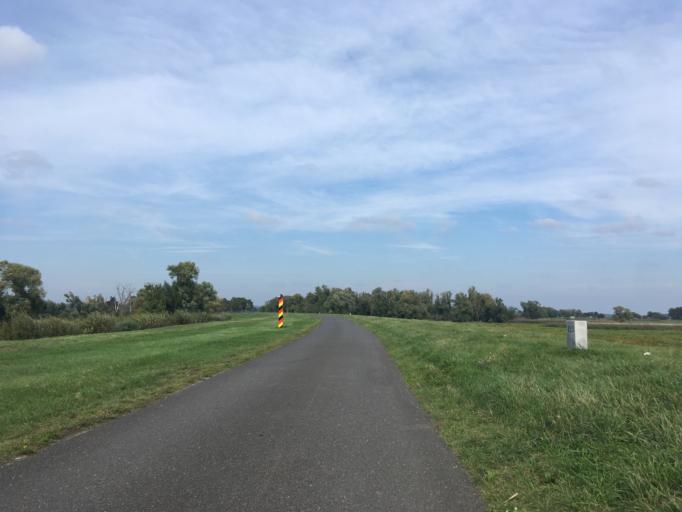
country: DE
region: Brandenburg
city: Schoneberg
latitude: 52.9398
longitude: 14.1377
